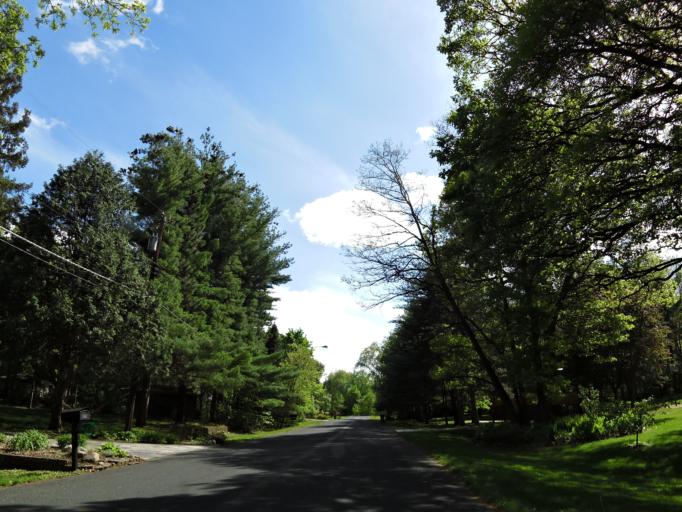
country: US
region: Minnesota
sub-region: Washington County
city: Lakeland
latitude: 44.9696
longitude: -92.7707
